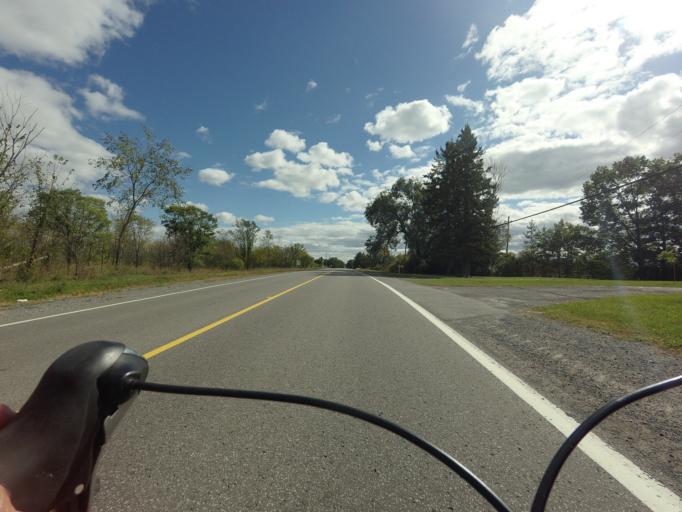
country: CA
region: Ontario
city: Bells Corners
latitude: 45.2141
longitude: -75.7109
